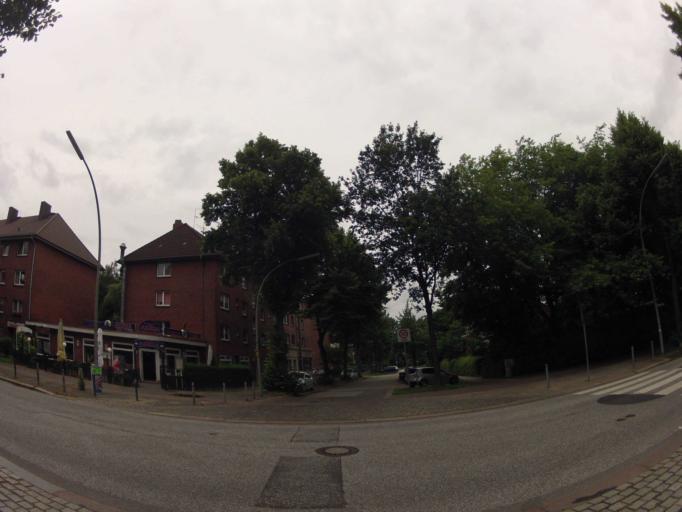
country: DE
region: Hamburg
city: Rothenburgsort
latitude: 53.5352
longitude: 10.0420
